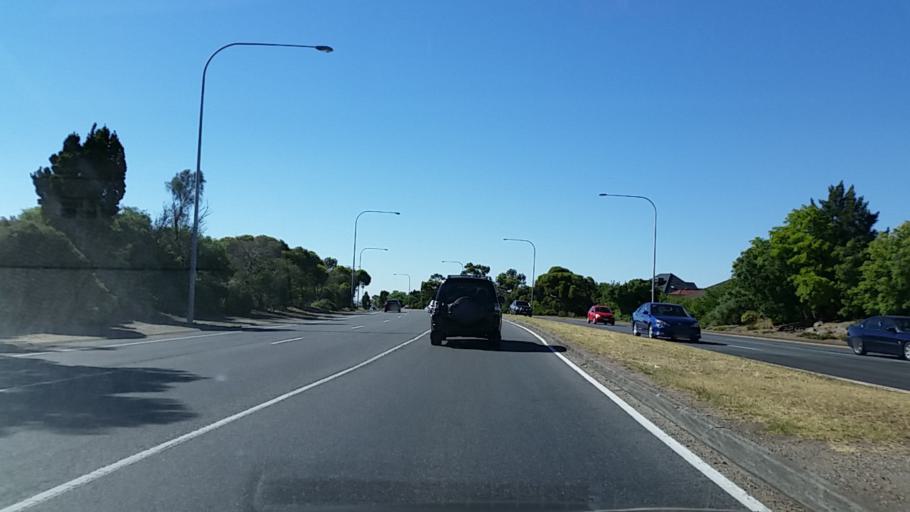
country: AU
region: South Australia
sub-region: Tea Tree Gully
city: Modbury
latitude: -34.8113
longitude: 138.6747
